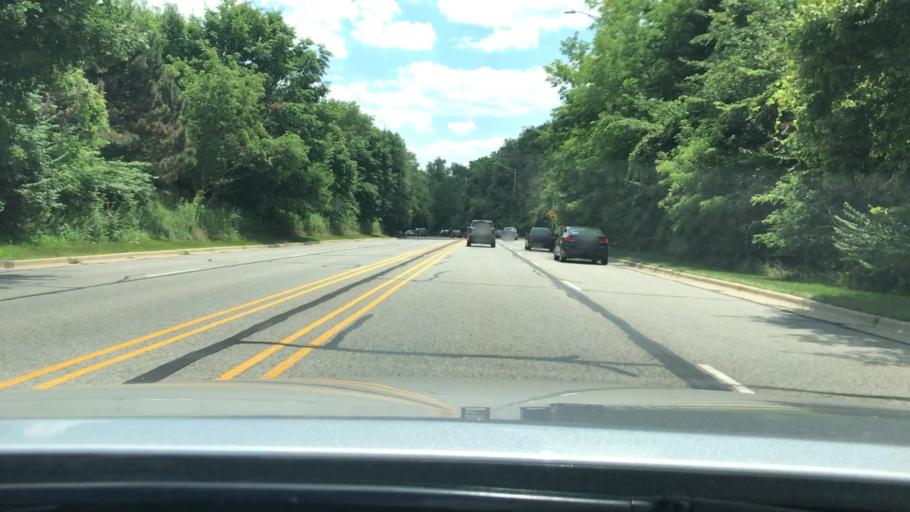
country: US
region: Illinois
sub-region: DuPage County
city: Naperville
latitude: 41.7898
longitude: -88.1173
